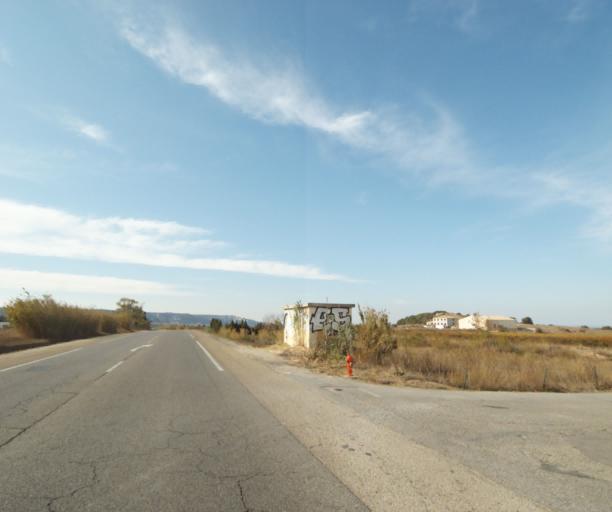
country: FR
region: Provence-Alpes-Cote d'Azur
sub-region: Departement des Bouches-du-Rhone
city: Gignac-la-Nerthe
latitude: 43.3839
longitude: 5.2062
